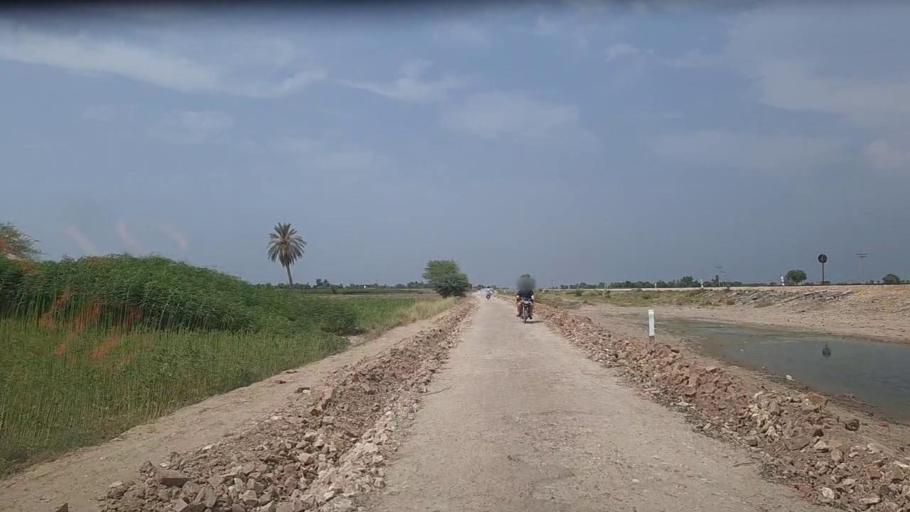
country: PK
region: Sindh
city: Bhiria
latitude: 26.9120
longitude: 68.2934
